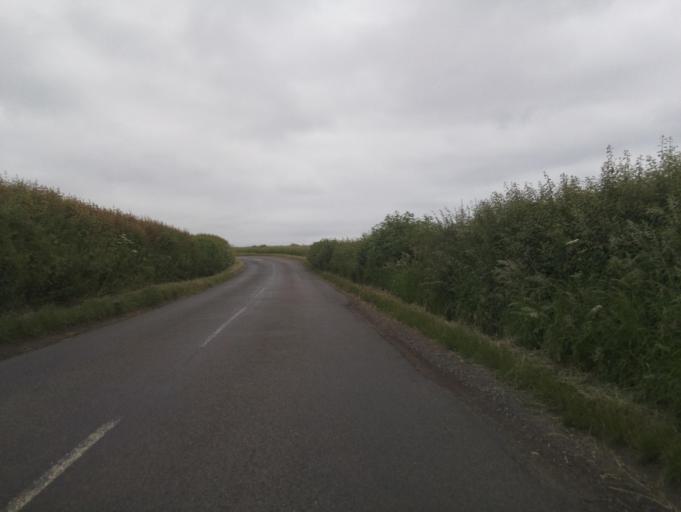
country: GB
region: England
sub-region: Leicestershire
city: Melton Mowbray
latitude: 52.6992
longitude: -0.8403
